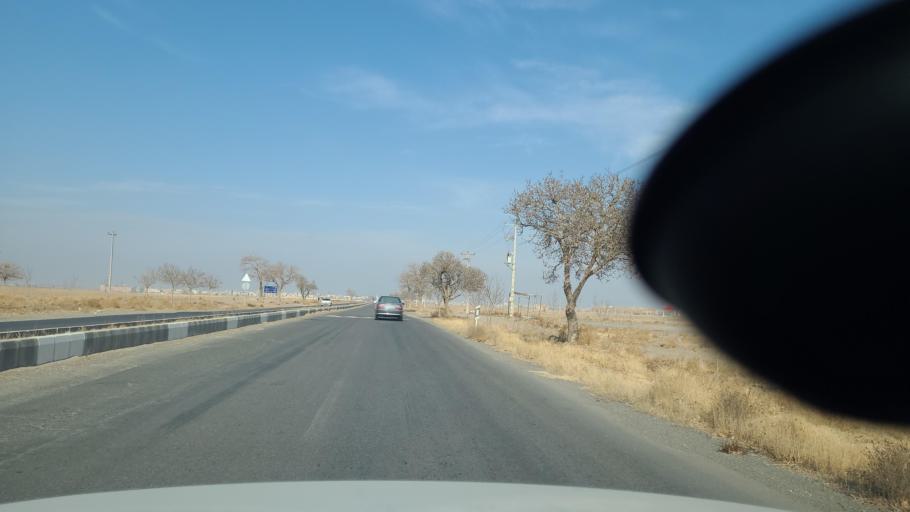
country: IR
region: Razavi Khorasan
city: Fariman
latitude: 35.6682
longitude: 59.8419
